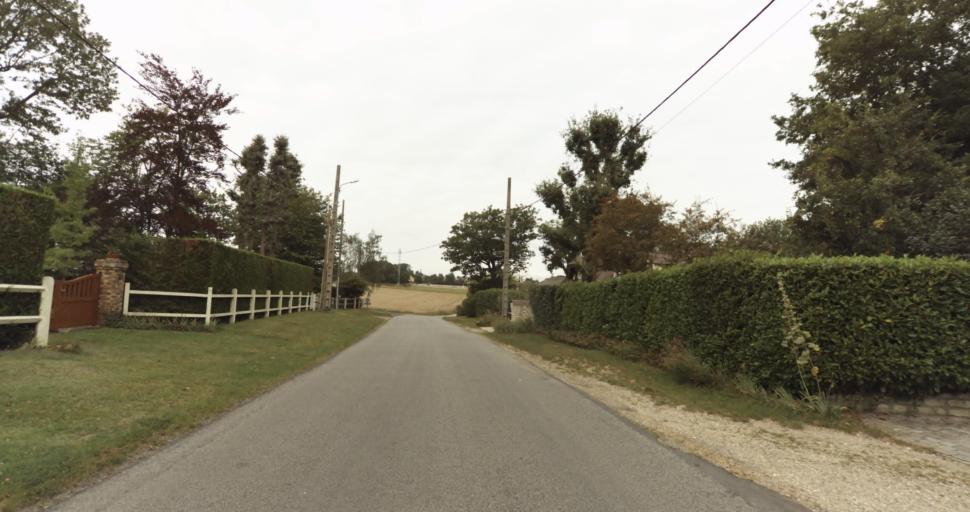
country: FR
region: Haute-Normandie
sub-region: Departement de l'Eure
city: Croth
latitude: 48.8694
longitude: 1.3565
